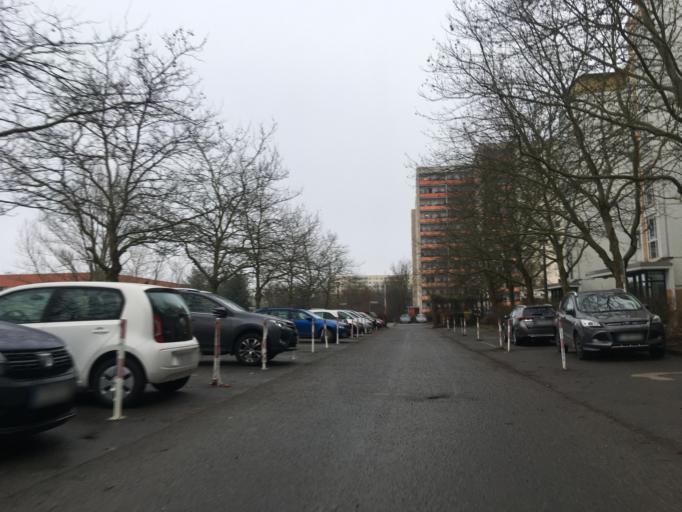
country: DE
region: Berlin
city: Buch
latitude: 52.6276
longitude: 13.4919
